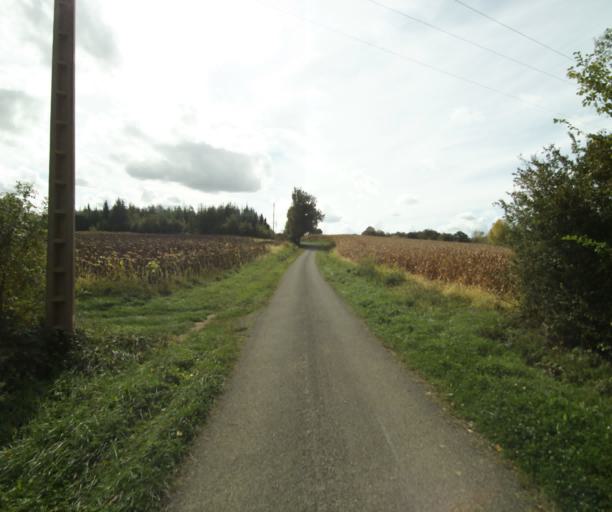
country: FR
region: Midi-Pyrenees
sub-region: Departement du Gers
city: Eauze
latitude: 43.8211
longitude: 0.1511
